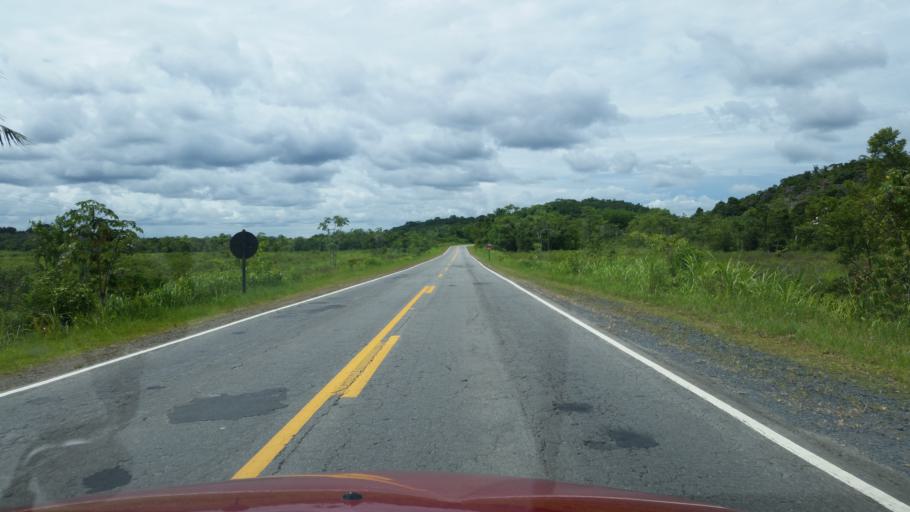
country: BR
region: Sao Paulo
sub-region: Juquia
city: Juquia
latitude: -24.3964
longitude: -47.5273
